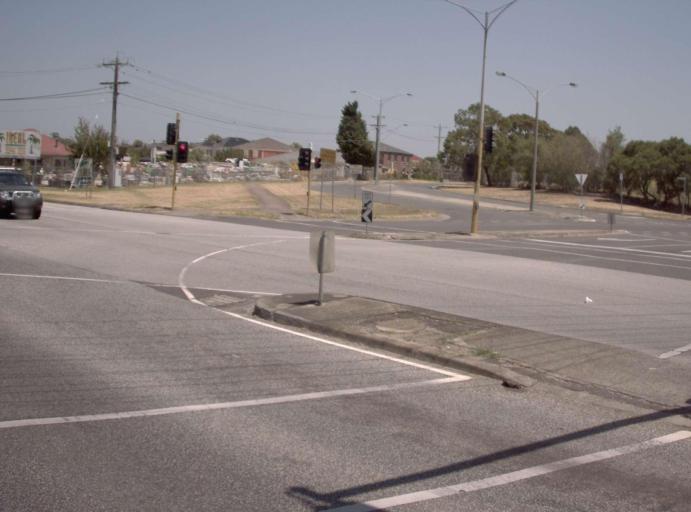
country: AU
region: Victoria
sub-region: Greater Dandenong
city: Springvale South
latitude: -37.9783
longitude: 145.1471
